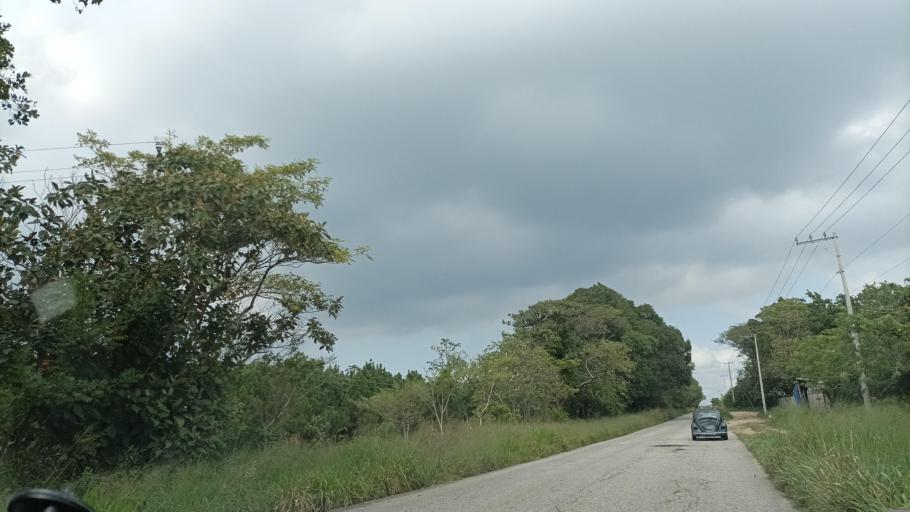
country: MX
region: Veracruz
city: Las Choapas
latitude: 17.8238
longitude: -94.1087
